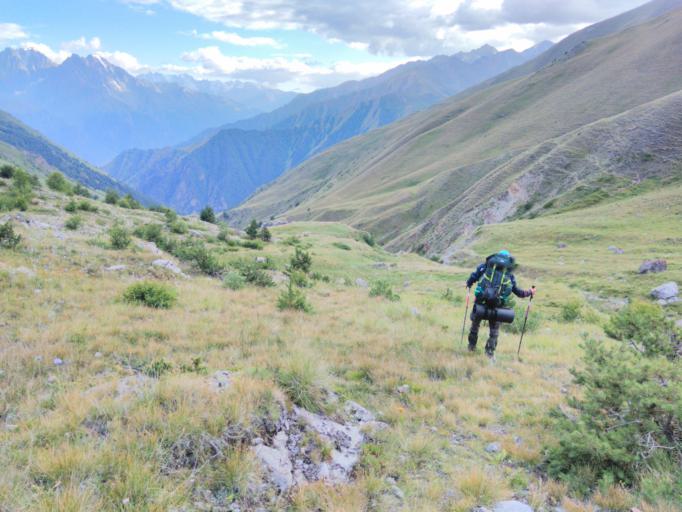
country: RU
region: Kabardino-Balkariya
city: Tyrnyauz
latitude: 43.3741
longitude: 42.7702
